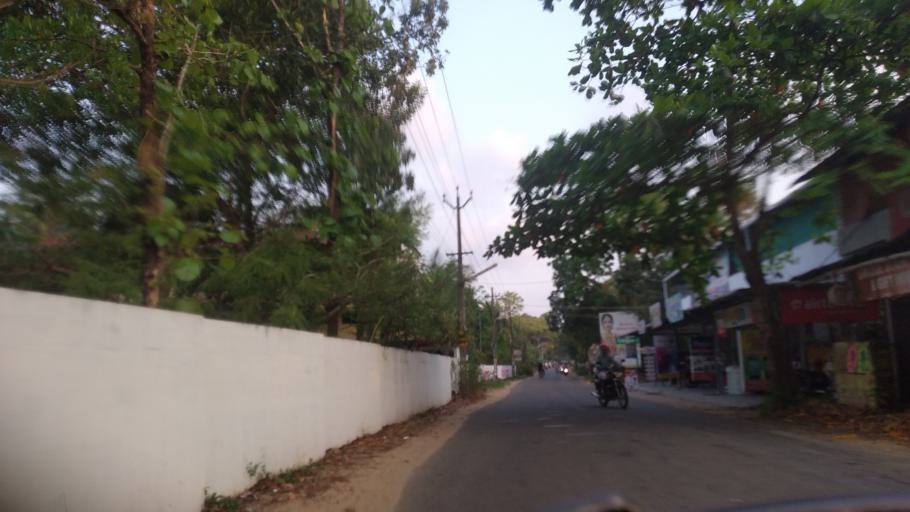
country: IN
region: Kerala
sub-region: Thrissur District
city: Kodungallur
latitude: 10.2641
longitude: 76.1433
